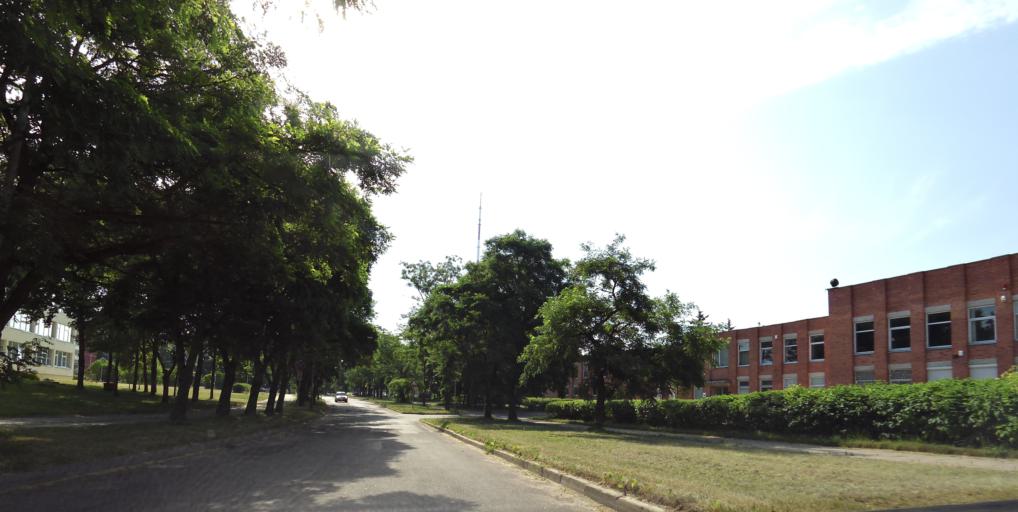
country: LT
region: Vilnius County
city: Pilaite
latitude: 54.6914
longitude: 25.2049
